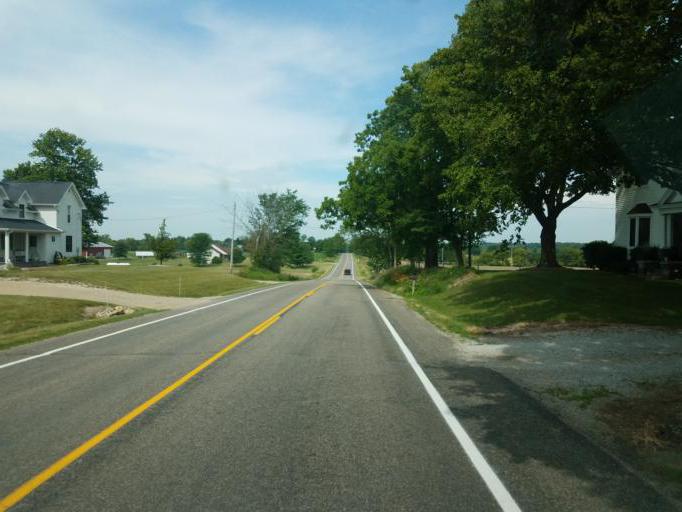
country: US
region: Michigan
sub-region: Eaton County
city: Charlotte
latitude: 42.6261
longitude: -84.8761
